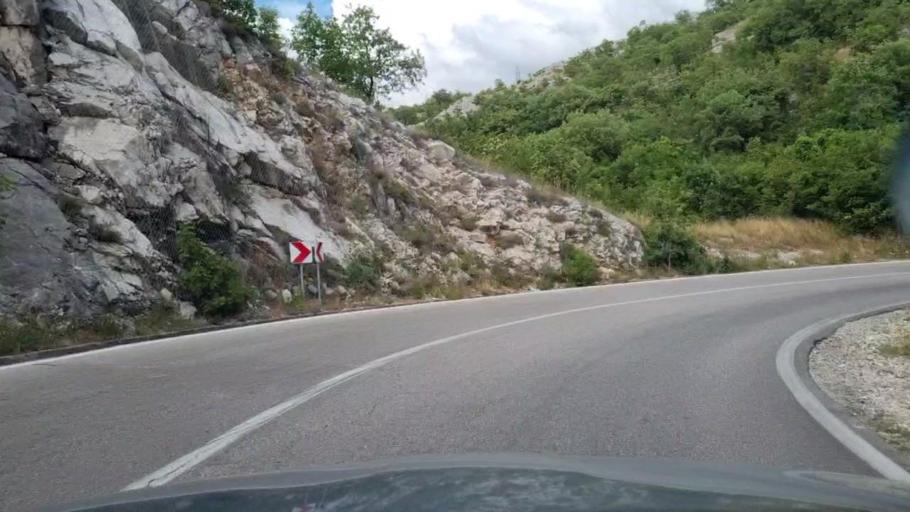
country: BA
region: Federation of Bosnia and Herzegovina
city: Blagaj
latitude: 43.2700
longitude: 17.9312
